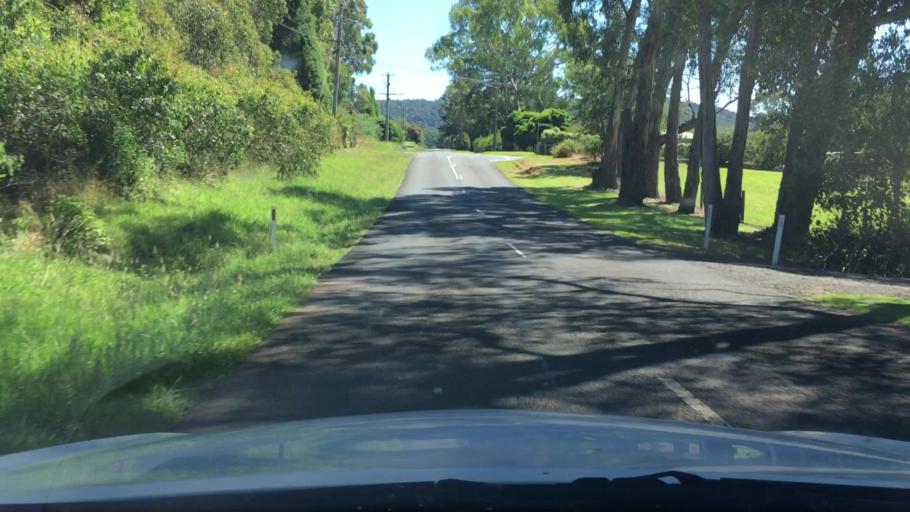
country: AU
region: Victoria
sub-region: Yarra Ranges
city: Mount Evelyn
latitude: -37.8000
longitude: 145.4192
